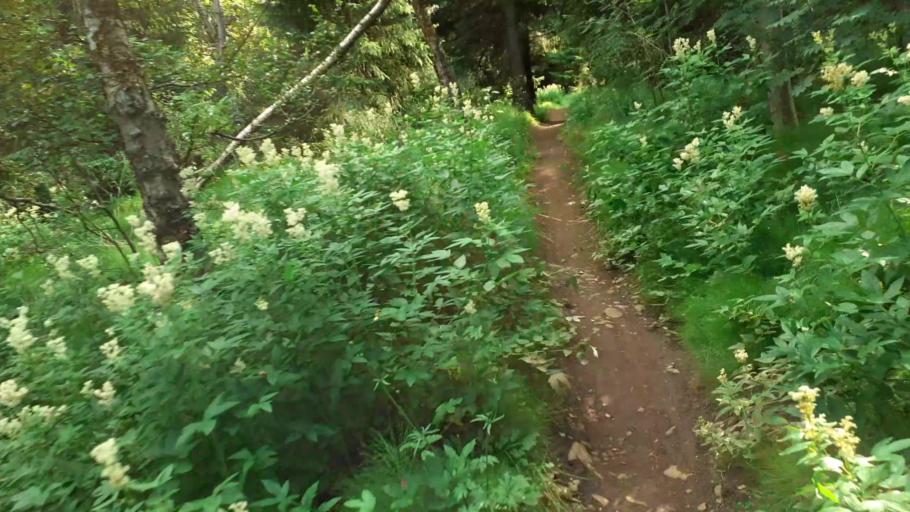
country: IS
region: Northeast
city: Akureyri
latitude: 65.6424
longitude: -18.0855
